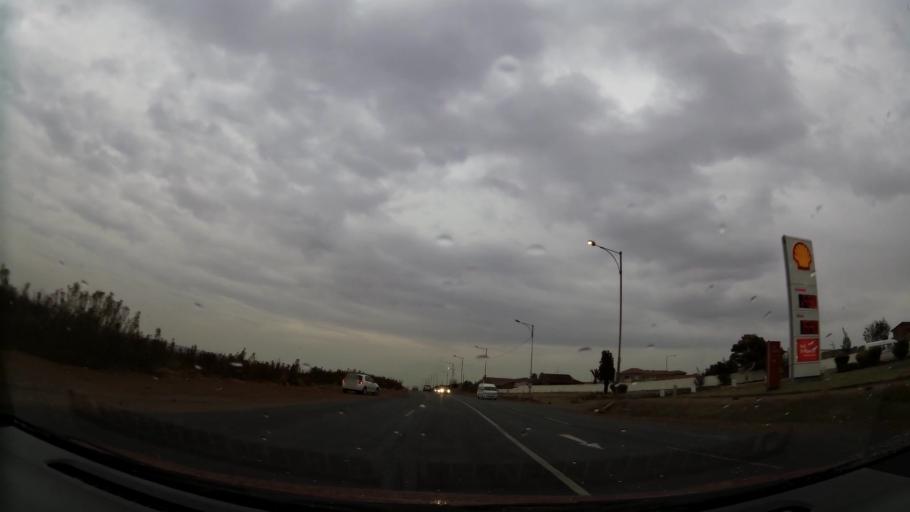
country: ZA
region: Gauteng
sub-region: City of Johannesburg Metropolitan Municipality
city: Roodepoort
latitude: -26.1649
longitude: 27.8063
